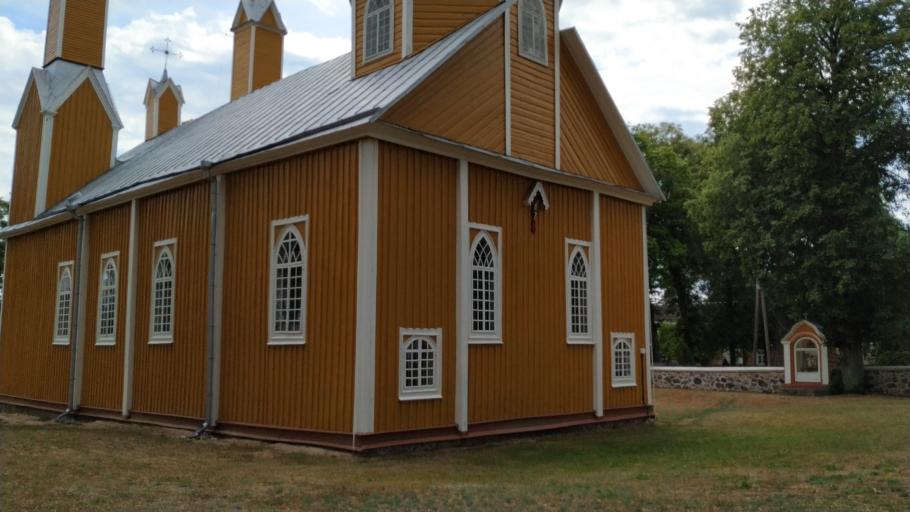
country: LT
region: Alytaus apskritis
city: Varena
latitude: 54.0711
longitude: 24.3898
